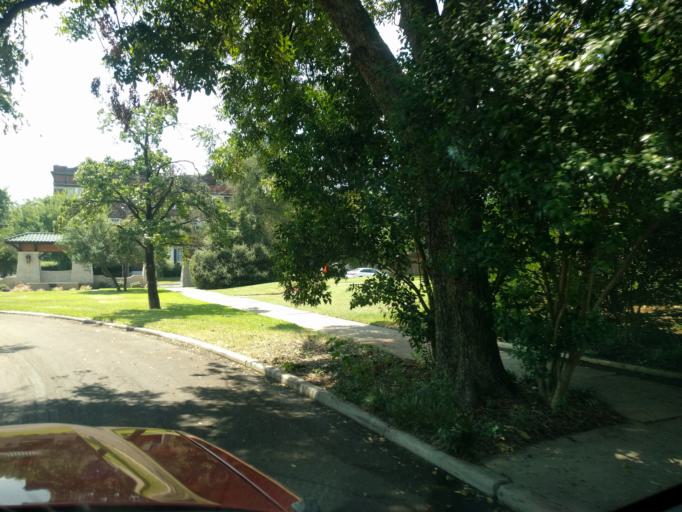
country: US
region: Texas
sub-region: Dallas County
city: Highland Park
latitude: 32.8018
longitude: -96.7704
